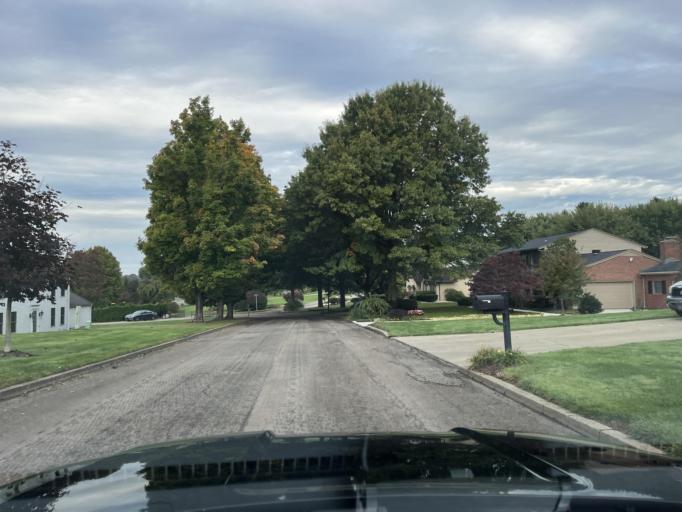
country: US
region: Pennsylvania
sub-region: Fayette County
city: Leith-Hatfield
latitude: 39.8783
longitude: -79.7239
